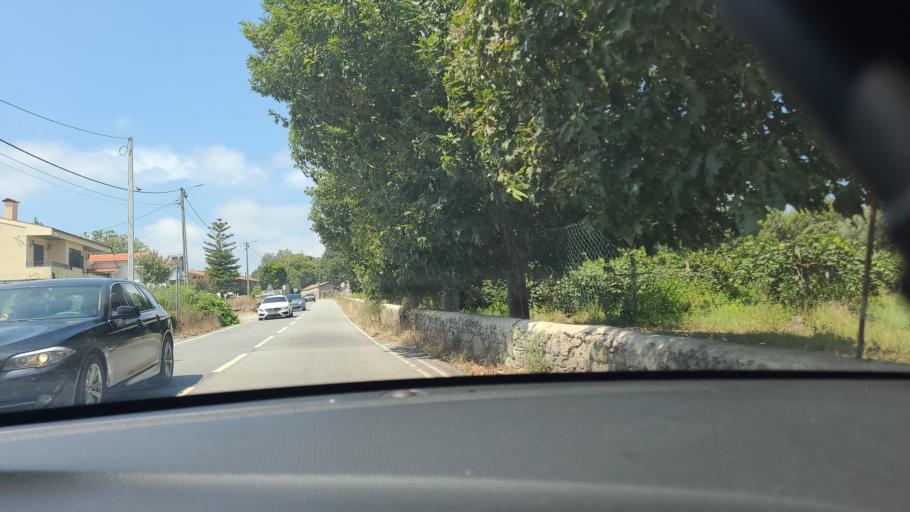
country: PT
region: Braga
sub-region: Amares
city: Amares
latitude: 41.6232
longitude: -8.3382
